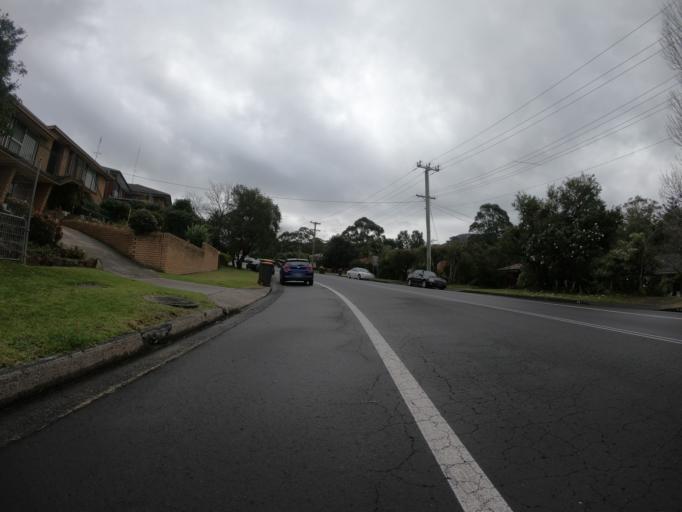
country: AU
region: New South Wales
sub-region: Wollongong
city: West Wollongong
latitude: -34.4266
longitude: 150.8567
